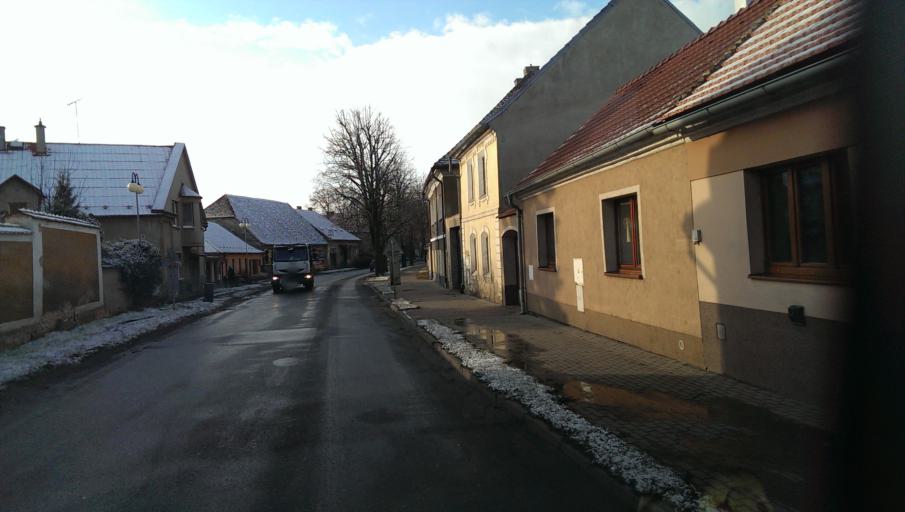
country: CZ
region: Ustecky
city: Budyne nad Ohri
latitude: 50.4054
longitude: 14.1316
